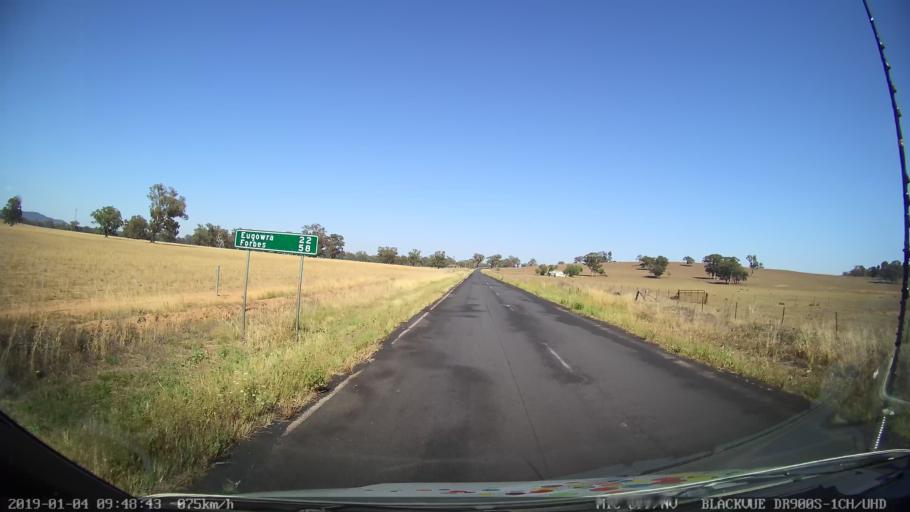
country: AU
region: New South Wales
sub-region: Cabonne
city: Canowindra
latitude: -33.5967
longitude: 148.4294
